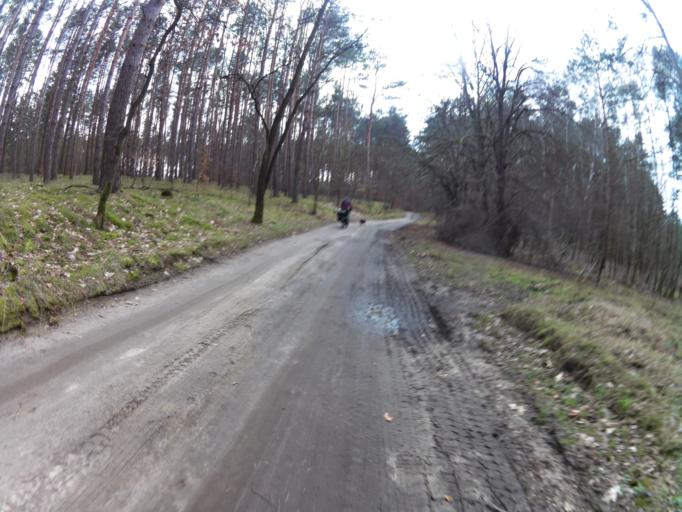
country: PL
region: Lubusz
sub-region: Powiat gorzowski
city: Lubiszyn
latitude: 52.7725
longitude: 14.8443
